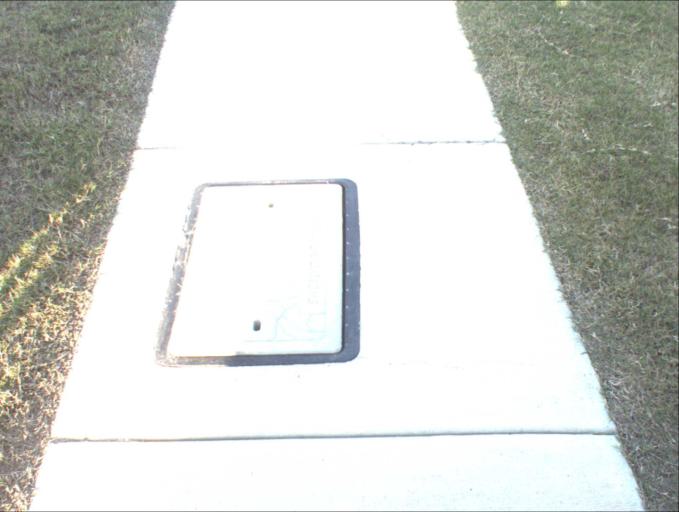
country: AU
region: Queensland
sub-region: Logan
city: Chambers Flat
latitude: -27.7713
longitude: 153.1103
